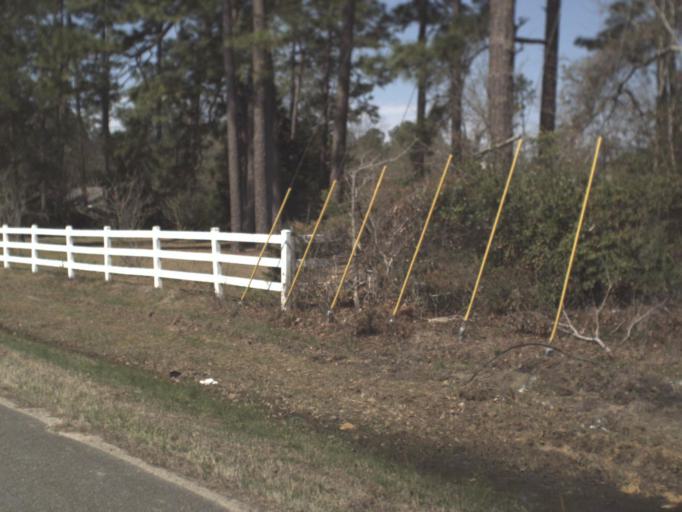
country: US
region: Florida
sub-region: Gadsden County
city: Gretna
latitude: 30.5929
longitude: -84.6696
